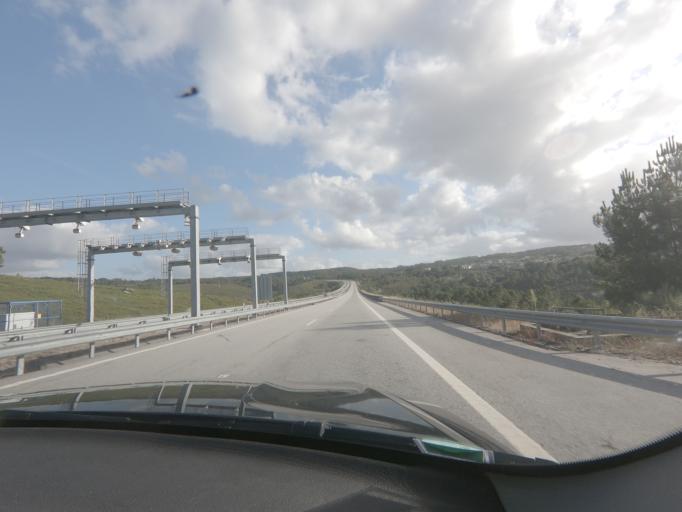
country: PT
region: Viseu
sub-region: Viseu
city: Campo
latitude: 40.7541
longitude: -7.9223
